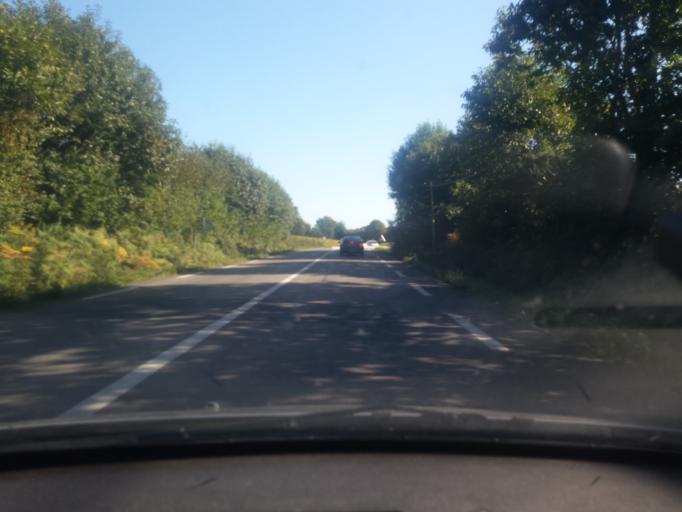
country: FR
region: Brittany
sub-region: Departement du Morbihan
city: Moreac
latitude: 47.9247
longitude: -2.8396
